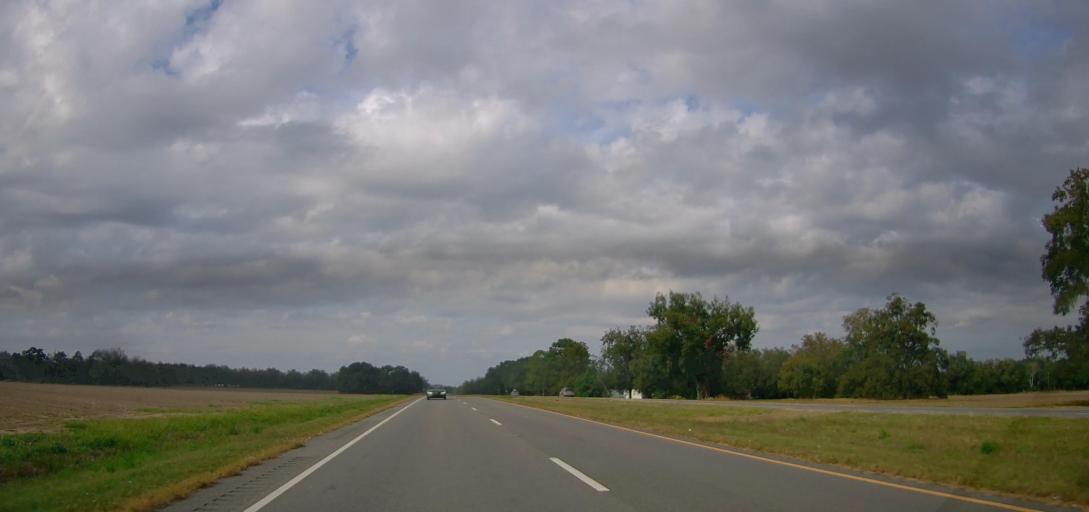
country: US
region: Georgia
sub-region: Thomas County
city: Meigs
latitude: 31.0292
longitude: -84.0619
